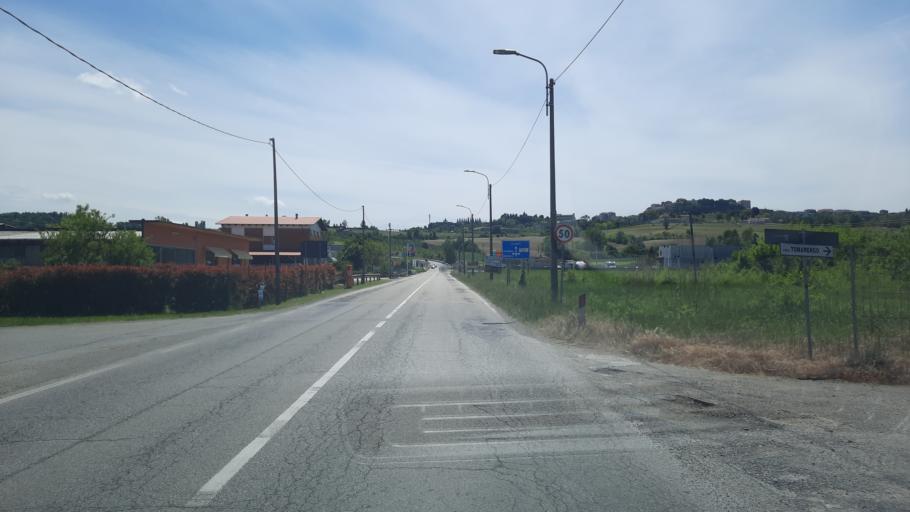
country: IT
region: Piedmont
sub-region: Provincia di Asti
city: Moncalvo
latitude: 45.0604
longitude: 8.2783
